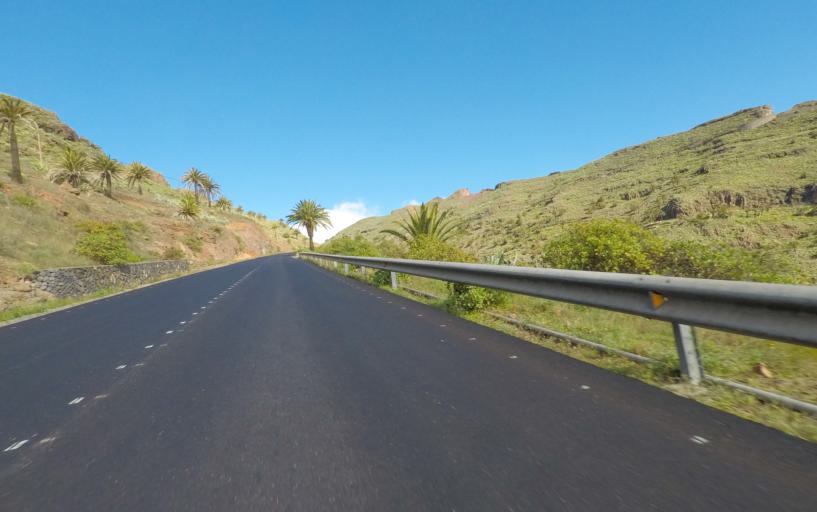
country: ES
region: Canary Islands
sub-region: Provincia de Santa Cruz de Tenerife
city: Alajero
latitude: 28.0695
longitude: -17.2068
